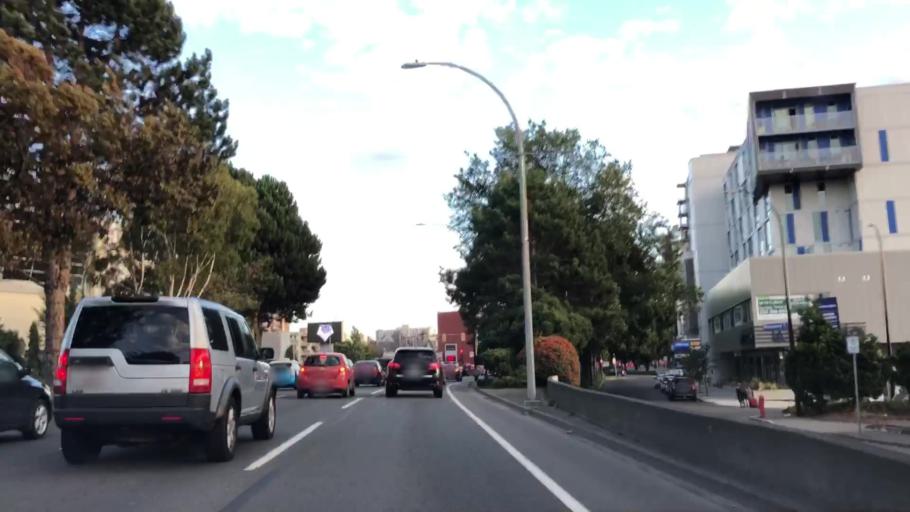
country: CA
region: British Columbia
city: Victoria
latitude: 48.4325
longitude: -123.3620
